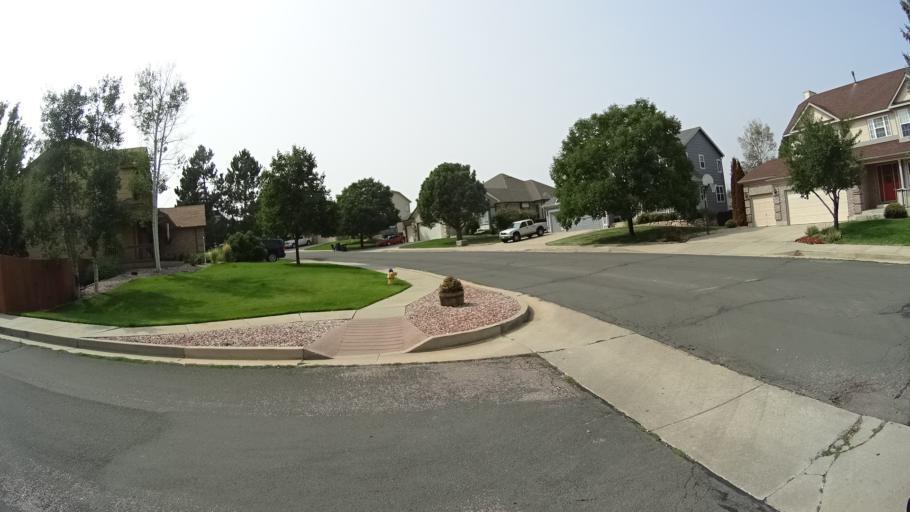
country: US
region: Colorado
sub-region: El Paso County
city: Cimarron Hills
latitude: 38.9199
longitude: -104.7471
